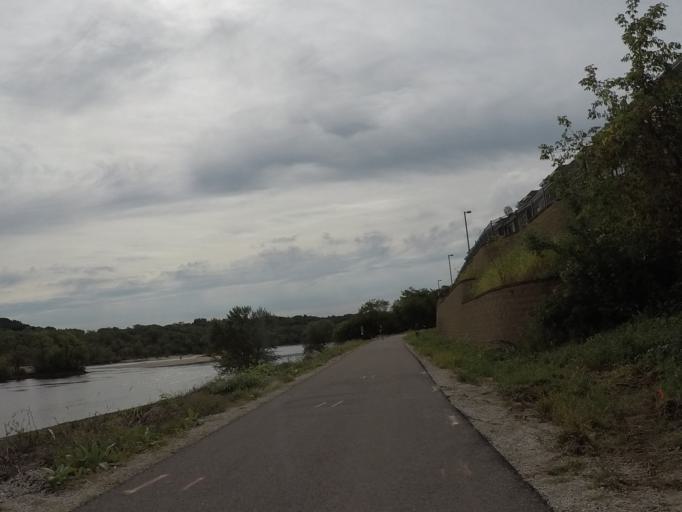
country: US
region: Wisconsin
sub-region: Sauk County
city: Prairie du Sac
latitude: 43.2909
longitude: -89.7200
